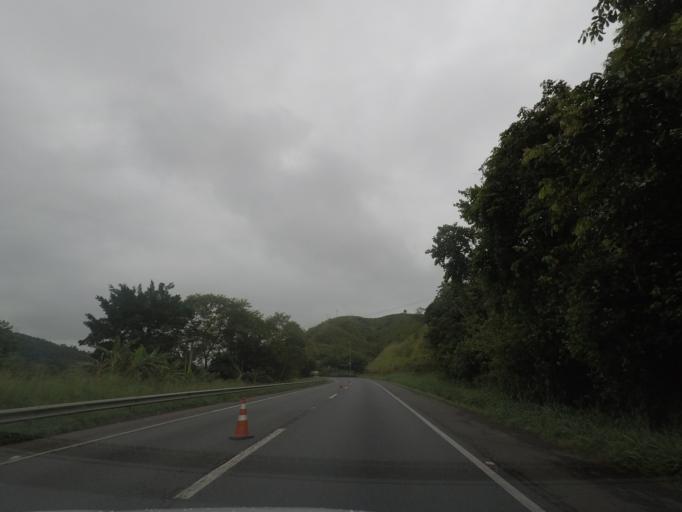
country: BR
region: Sao Paulo
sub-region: Cajati
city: Cajati
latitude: -24.8032
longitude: -48.2113
